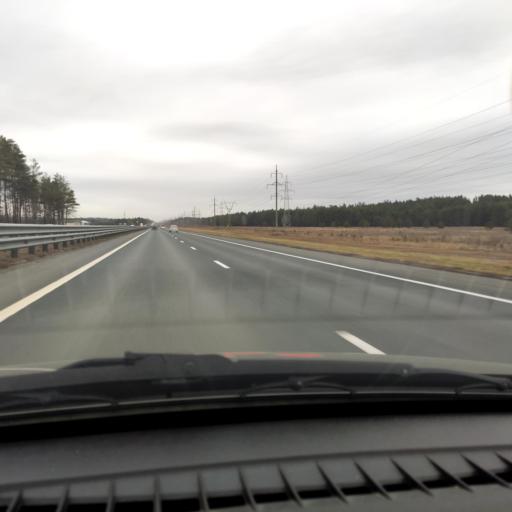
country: RU
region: Samara
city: Povolzhskiy
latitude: 53.5144
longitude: 49.6661
